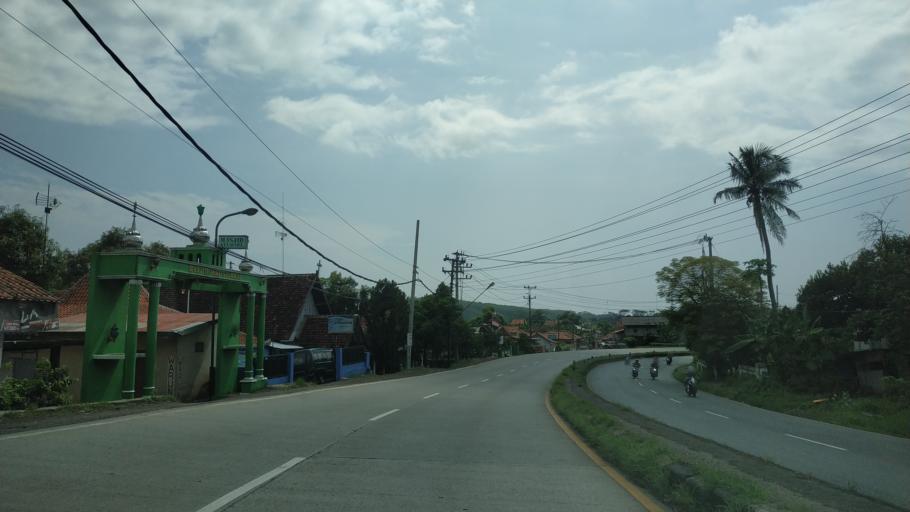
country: ID
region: Central Java
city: Pekalongan
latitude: -6.9455
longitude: 109.8087
